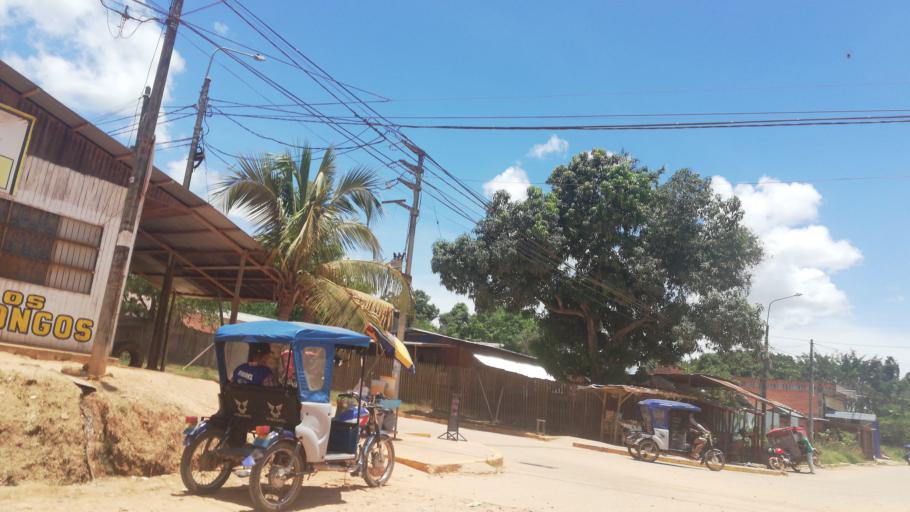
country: PE
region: Ucayali
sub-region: Provincia de Coronel Portillo
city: Puerto Callao
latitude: -8.3595
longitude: -74.5826
